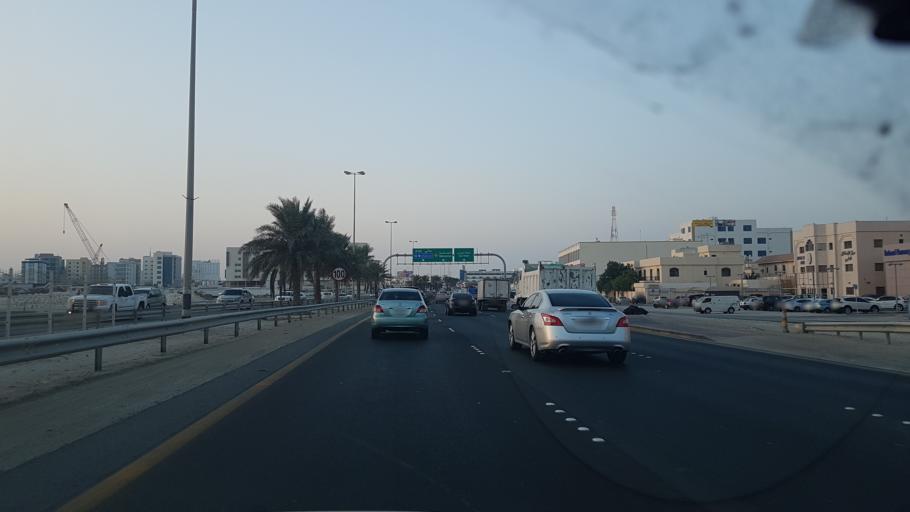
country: BH
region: Northern
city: Ar Rifa'
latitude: 26.1453
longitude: 50.5775
